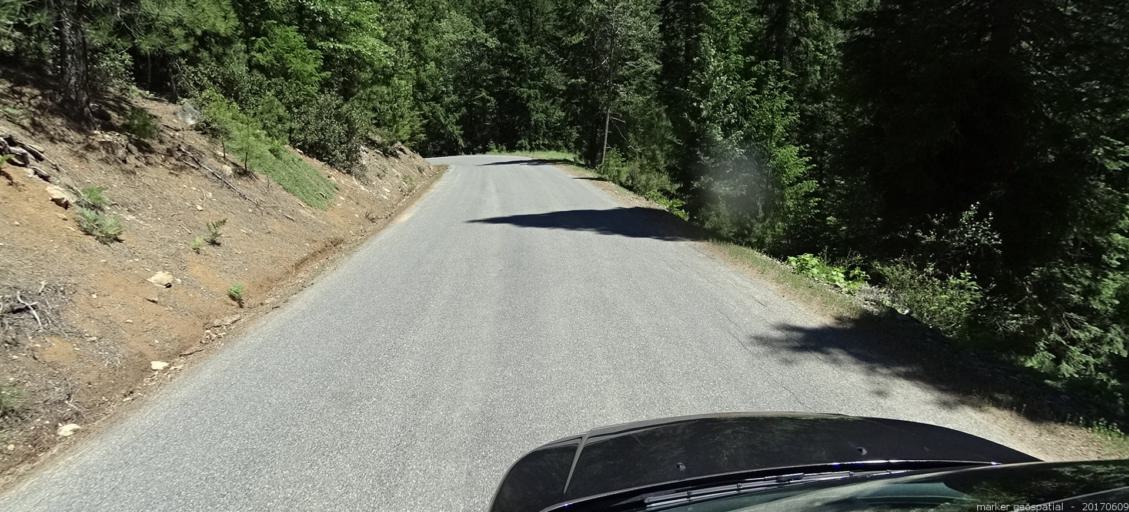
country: US
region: California
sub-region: Siskiyou County
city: Yreka
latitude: 41.4287
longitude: -122.9507
